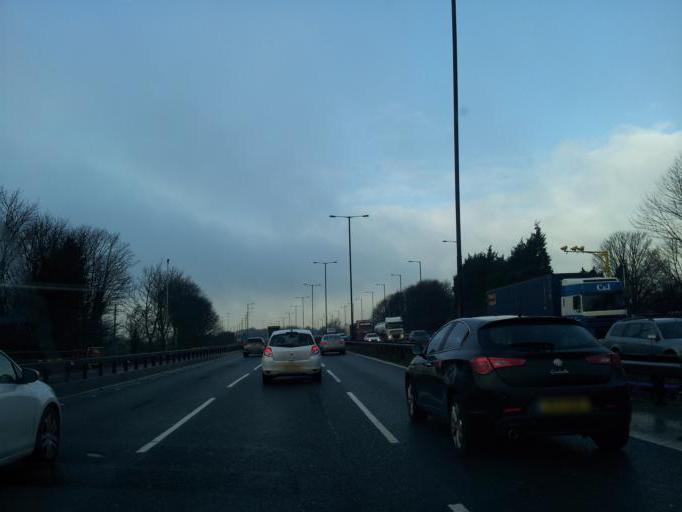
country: GB
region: England
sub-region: Manchester
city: Heywood
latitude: 53.5710
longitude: -2.2218
